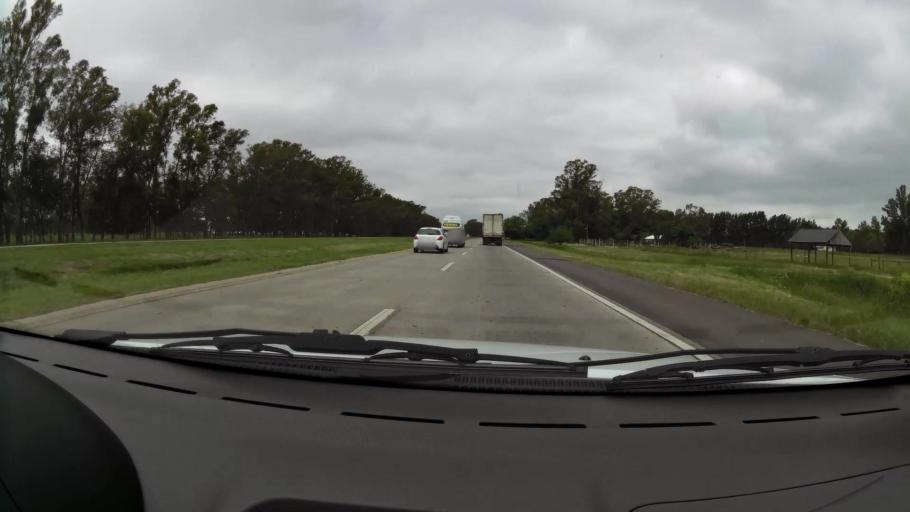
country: AR
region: Buenos Aires
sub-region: Partido de San Vicente
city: San Vicente
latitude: -35.0177
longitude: -58.2816
